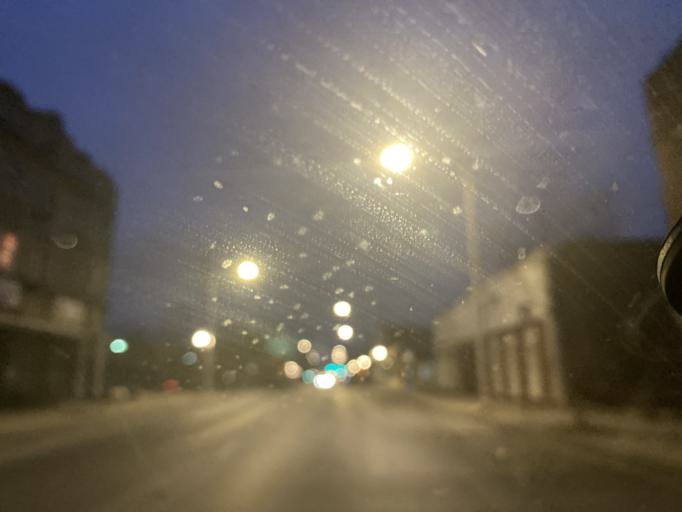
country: US
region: Illinois
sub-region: Cook County
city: Evergreen Park
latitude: 41.7795
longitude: -87.6624
